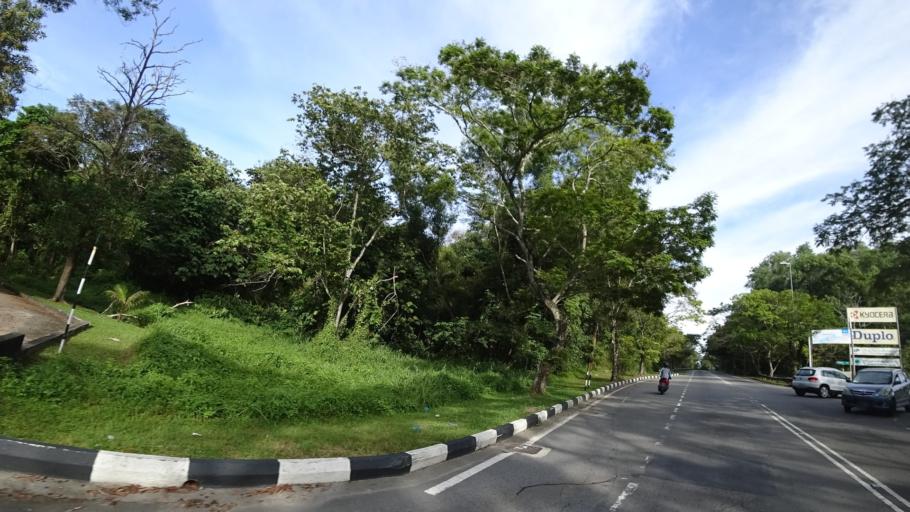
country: BN
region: Brunei and Muara
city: Bandar Seri Begawan
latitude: 4.8799
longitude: 114.8938
